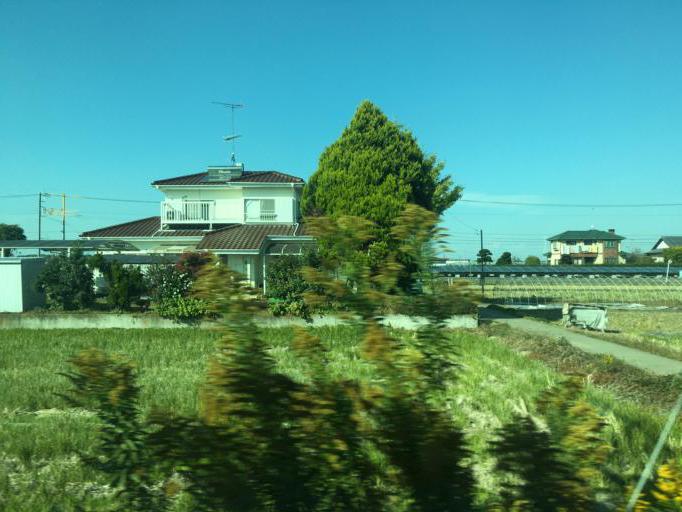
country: JP
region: Ibaraki
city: Shimodate
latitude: 36.3214
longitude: 140.0269
